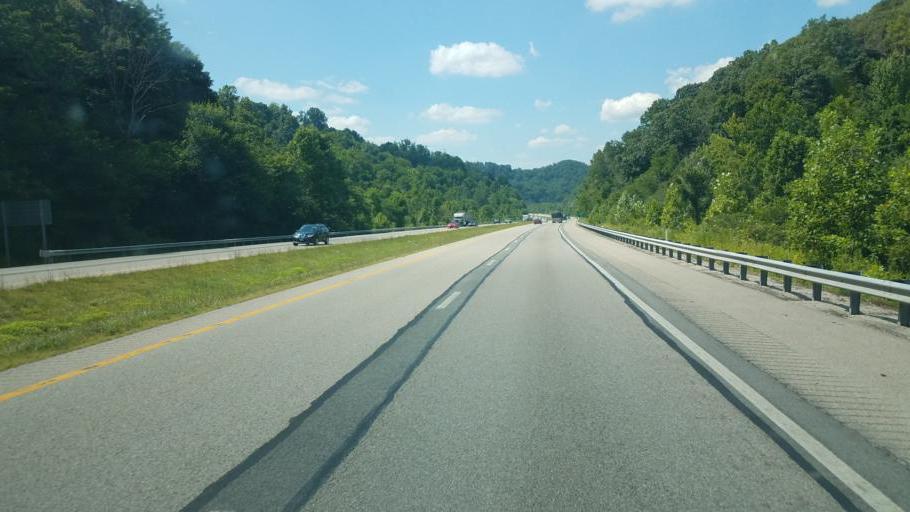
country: US
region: West Virginia
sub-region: Kanawha County
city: Sissonville
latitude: 38.4543
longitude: -81.6370
